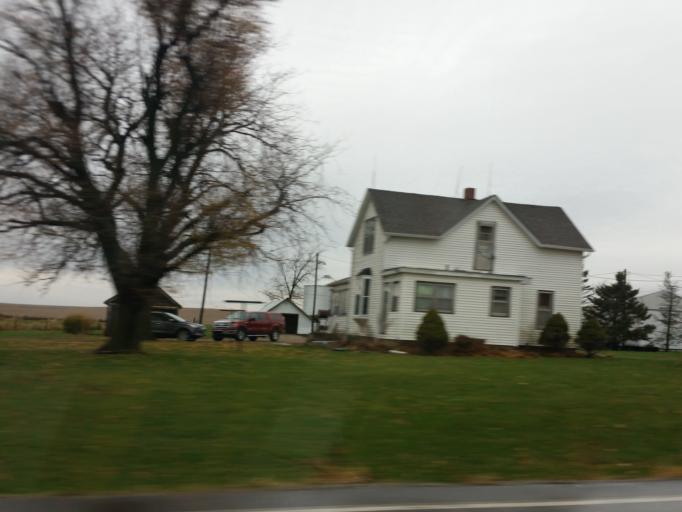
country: US
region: Iowa
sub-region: Benton County
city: Vinton
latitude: 42.0383
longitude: -92.0289
